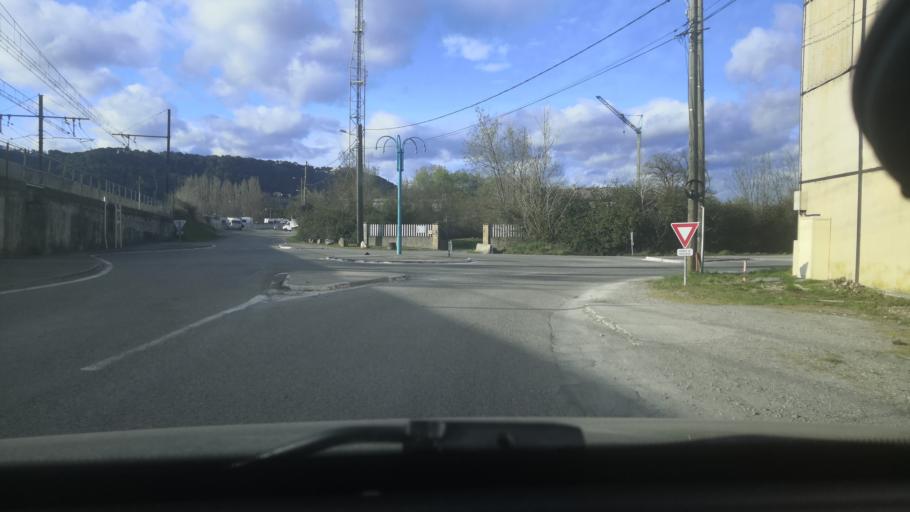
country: FR
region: Rhone-Alpes
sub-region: Departement de l'Ardeche
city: Le Teil
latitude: 44.5416
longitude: 4.6892
